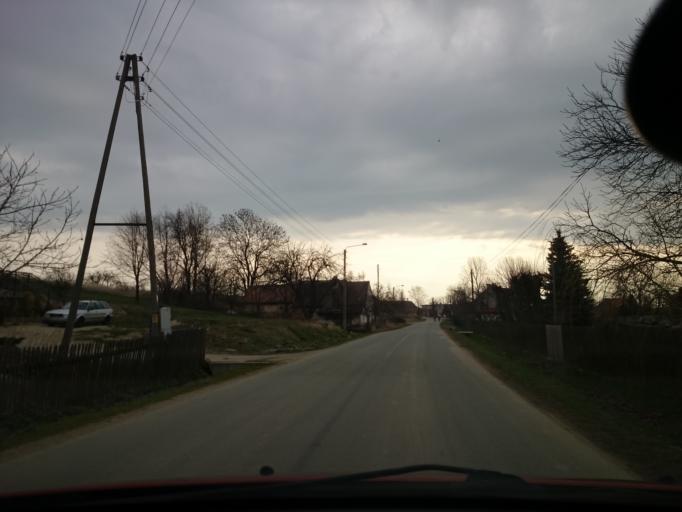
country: PL
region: Lower Silesian Voivodeship
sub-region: Powiat zabkowicki
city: Bardo
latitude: 50.5276
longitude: 16.7619
